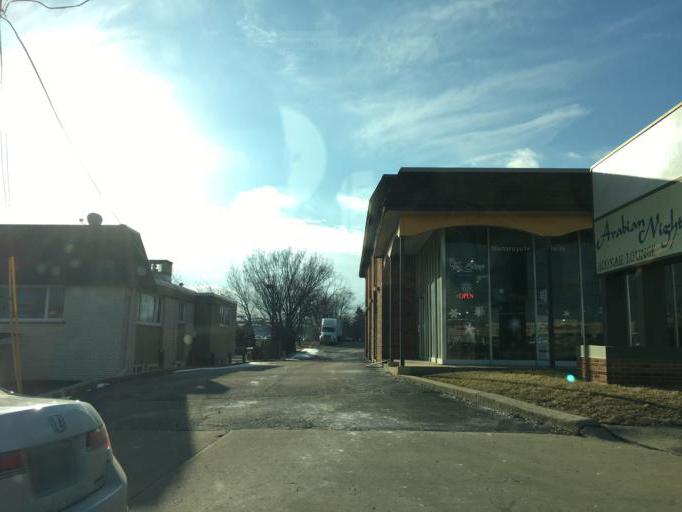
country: US
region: Illinois
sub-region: Cook County
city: Hoffman Estates
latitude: 42.0506
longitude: -88.0799
